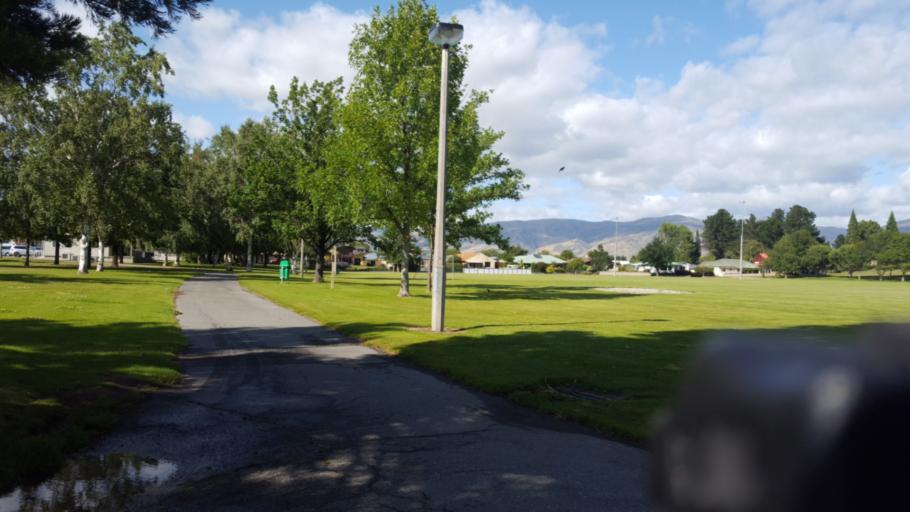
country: NZ
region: Otago
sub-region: Queenstown-Lakes District
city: Wanaka
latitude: -45.0428
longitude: 169.1945
